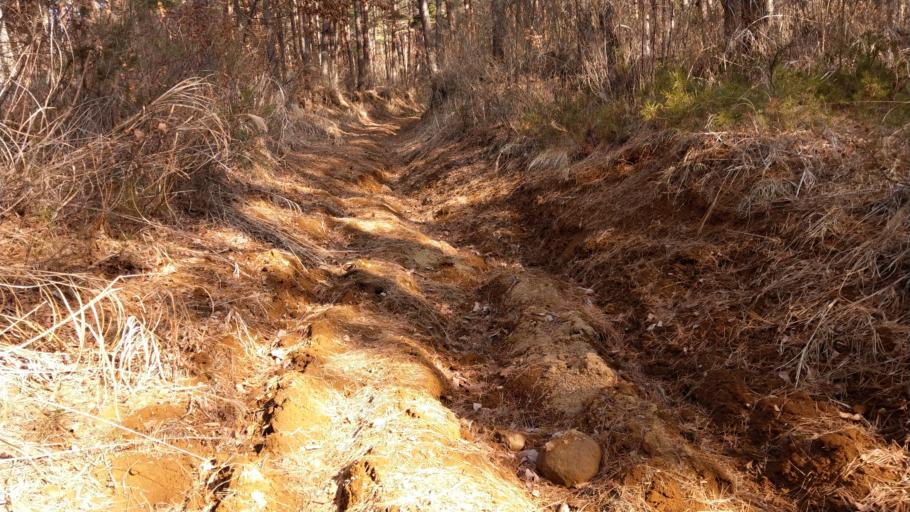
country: JP
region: Nagano
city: Komoro
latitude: 36.3655
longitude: 138.4331
